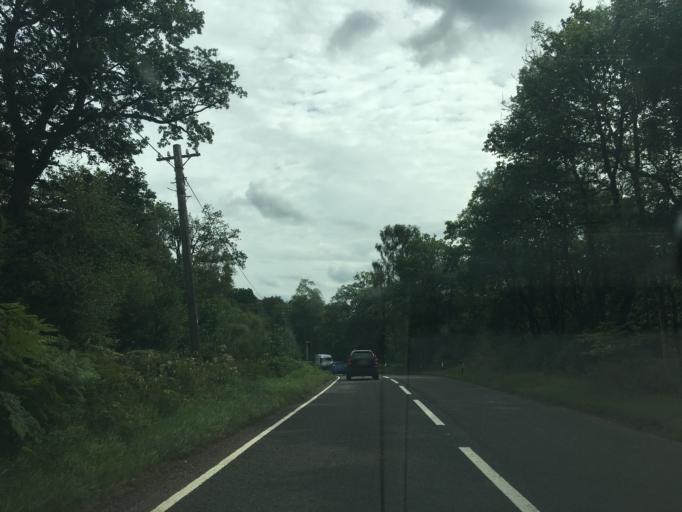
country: GB
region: Scotland
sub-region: Stirling
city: Callander
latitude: 56.2518
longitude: -4.2644
